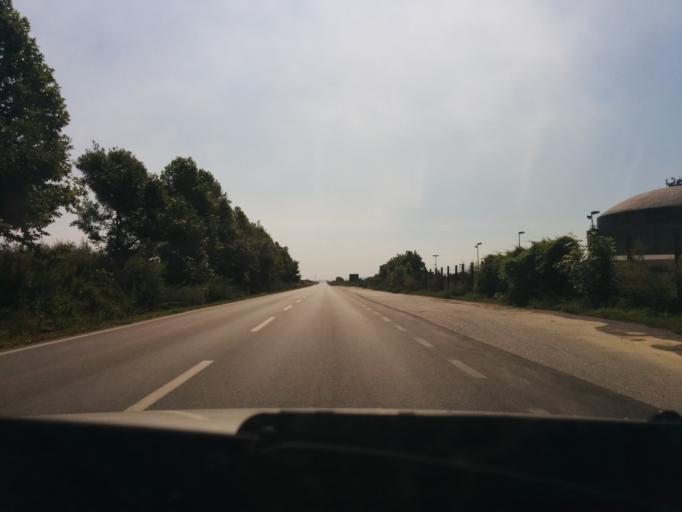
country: HR
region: Sisacko-Moslavacka
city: Husain
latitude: 45.4679
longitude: 16.8046
